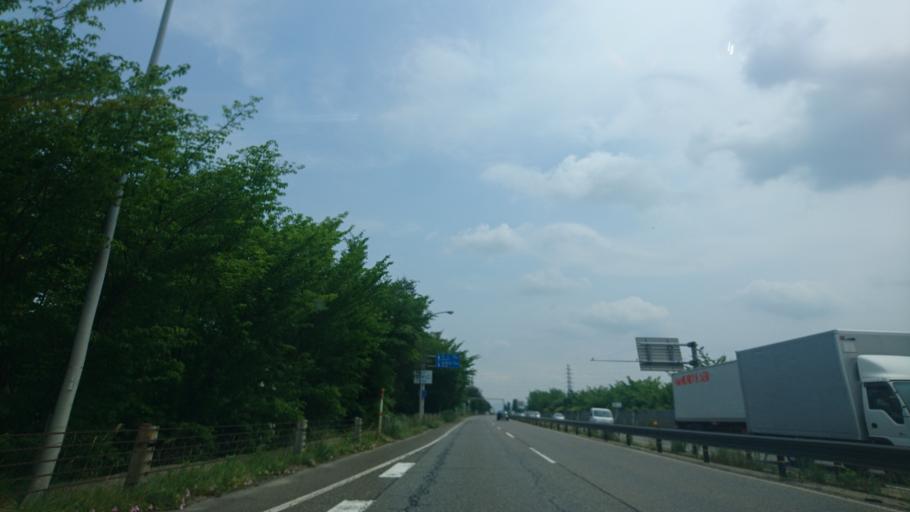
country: JP
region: Niigata
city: Kameda-honcho
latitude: 37.9445
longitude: 139.1885
